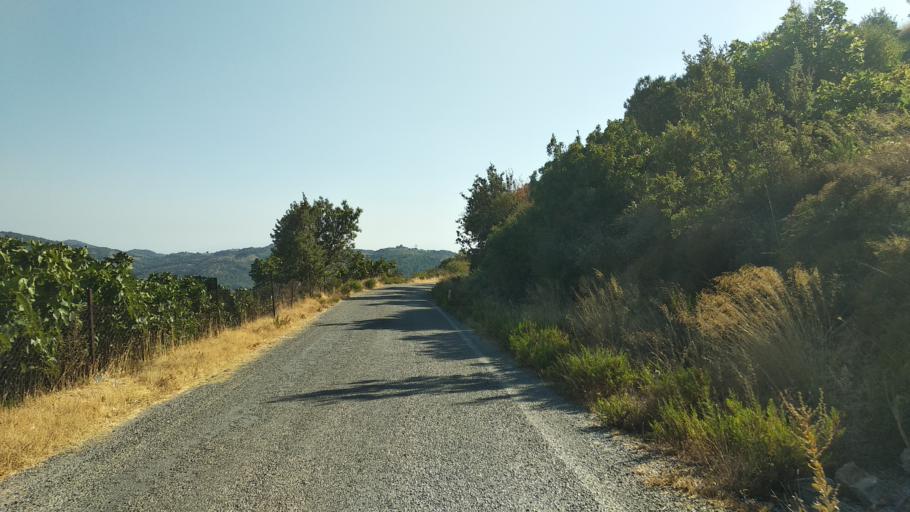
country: TR
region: Izmir
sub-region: Seferihisar
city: Seferhisar
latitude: 38.3200
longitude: 26.9293
